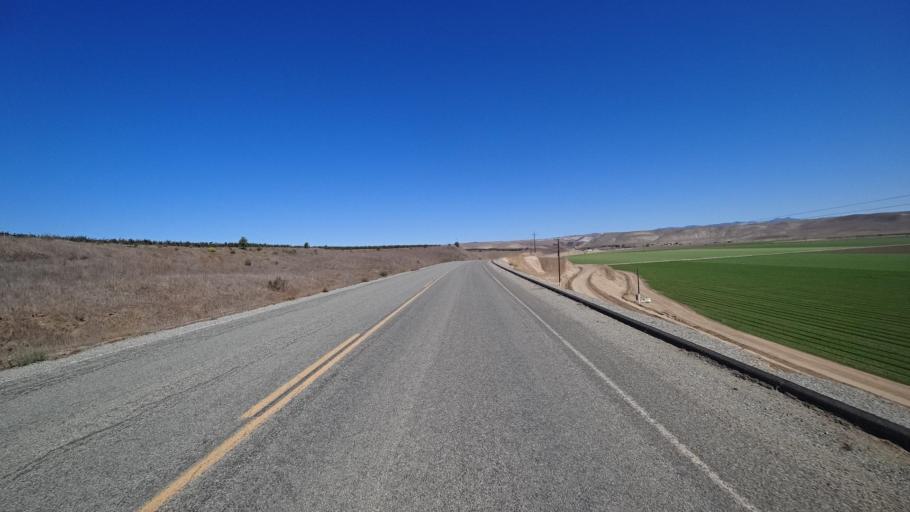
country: US
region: California
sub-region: Monterey County
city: King City
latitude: 36.2425
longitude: -121.1014
